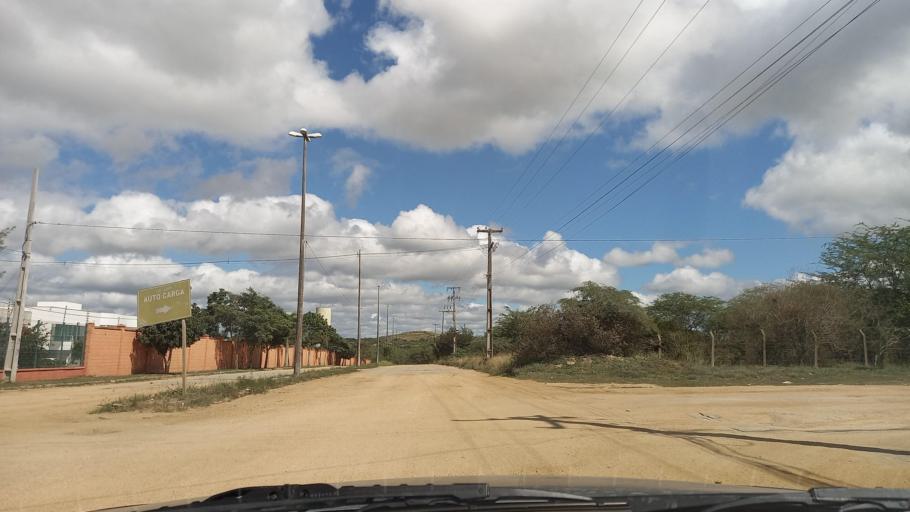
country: BR
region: Pernambuco
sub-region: Caruaru
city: Caruaru
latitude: -8.2421
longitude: -35.9816
